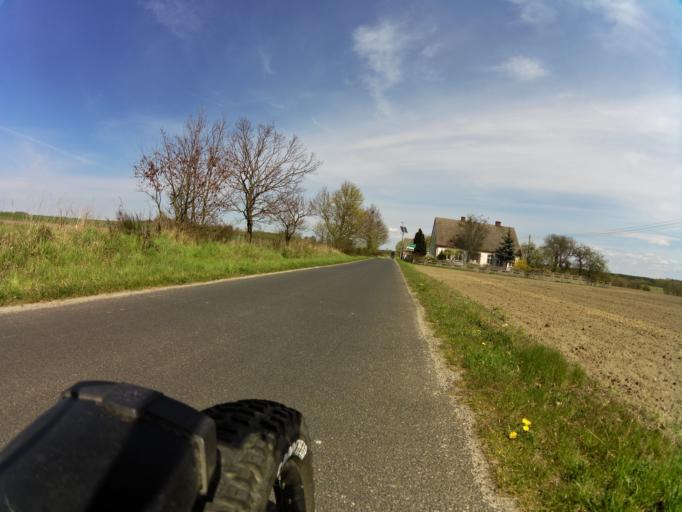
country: PL
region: West Pomeranian Voivodeship
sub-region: Powiat lobeski
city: Resko
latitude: 53.7914
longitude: 15.4301
